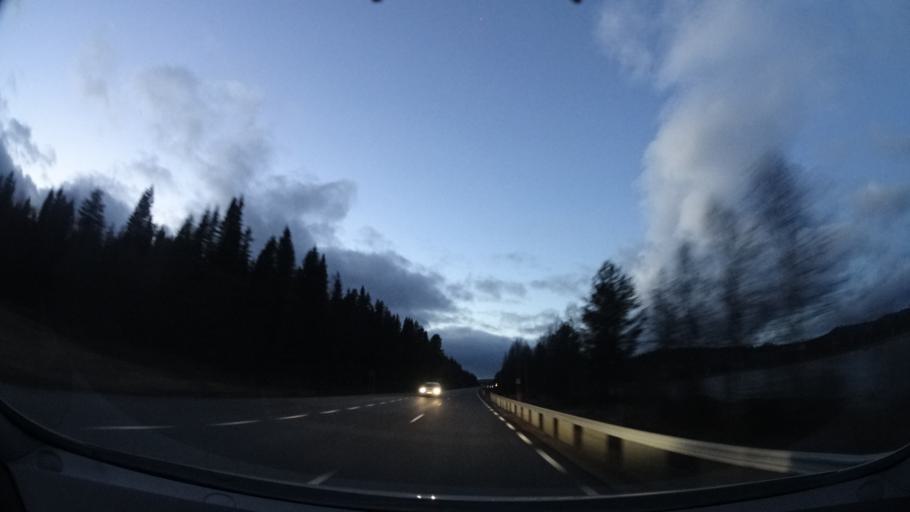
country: SE
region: Vaesterbotten
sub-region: Dorotea Kommun
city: Dorotea
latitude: 64.2325
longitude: 16.8064
